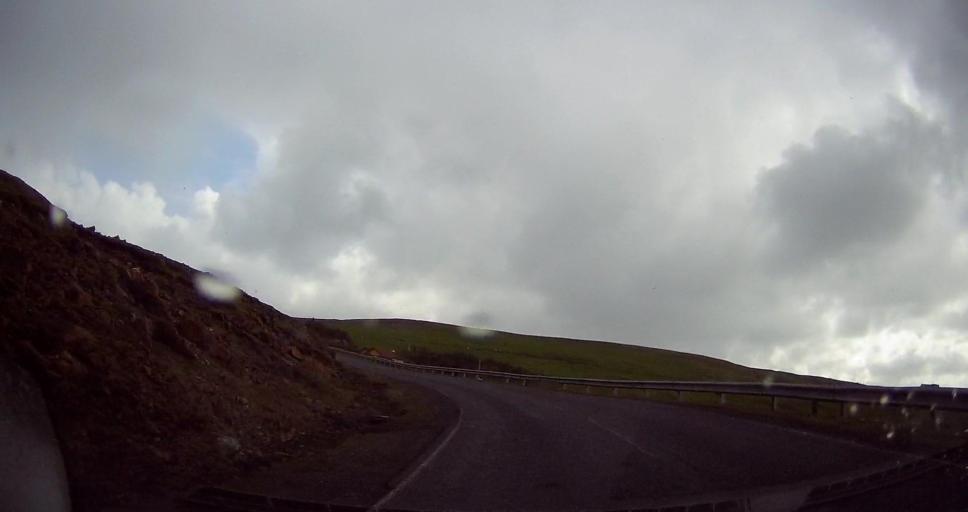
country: GB
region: Scotland
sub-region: Shetland Islands
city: Lerwick
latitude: 60.5412
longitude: -1.3508
